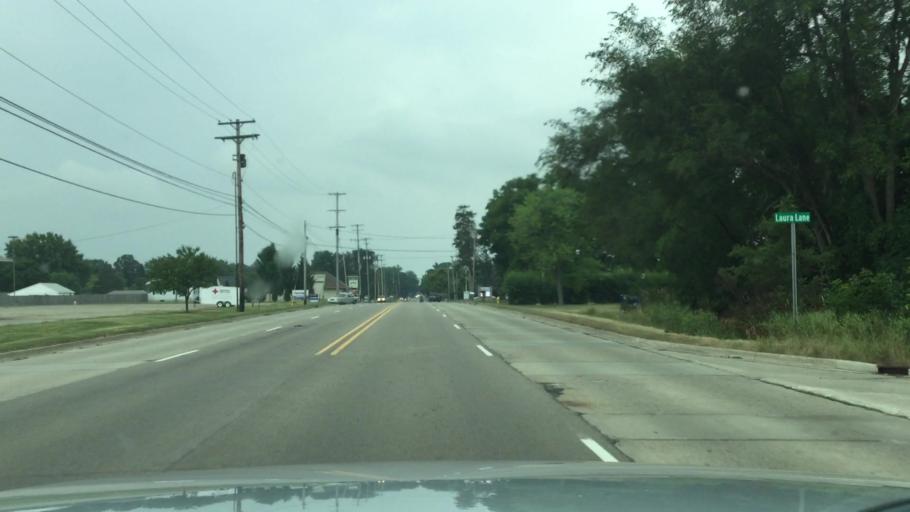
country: US
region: Michigan
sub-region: Shiawassee County
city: Owosso
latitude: 43.0179
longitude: -84.1768
